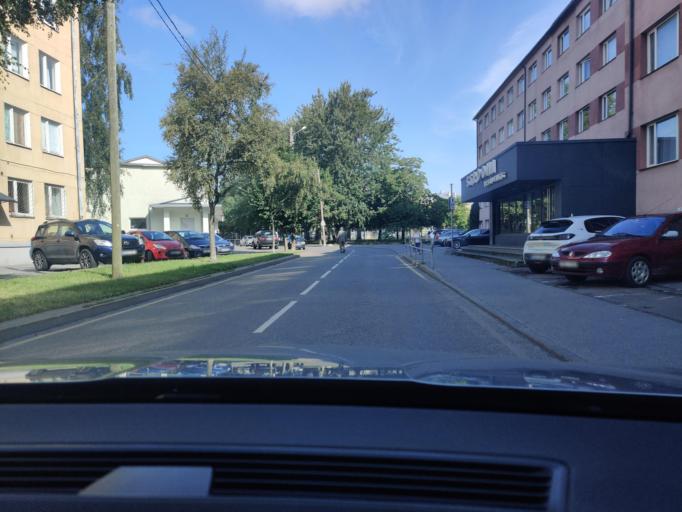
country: EE
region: Harju
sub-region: Tallinna linn
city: Tallinn
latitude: 59.4487
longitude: 24.6907
